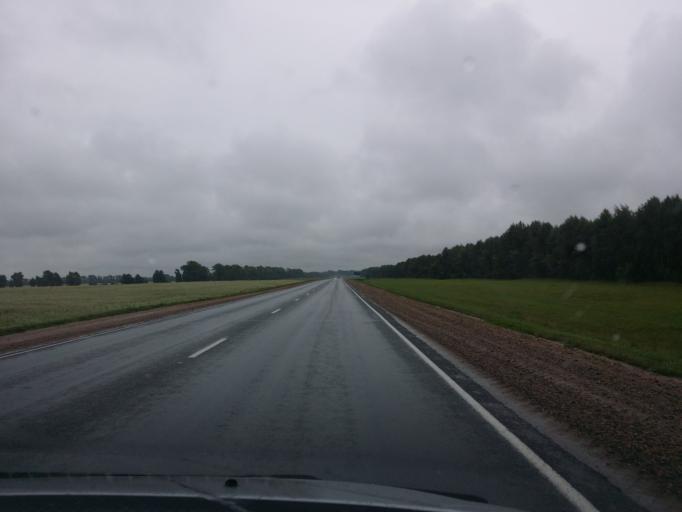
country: RU
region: Altai Krai
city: Bayunovskiye Klyuchi
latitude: 53.2947
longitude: 84.2967
